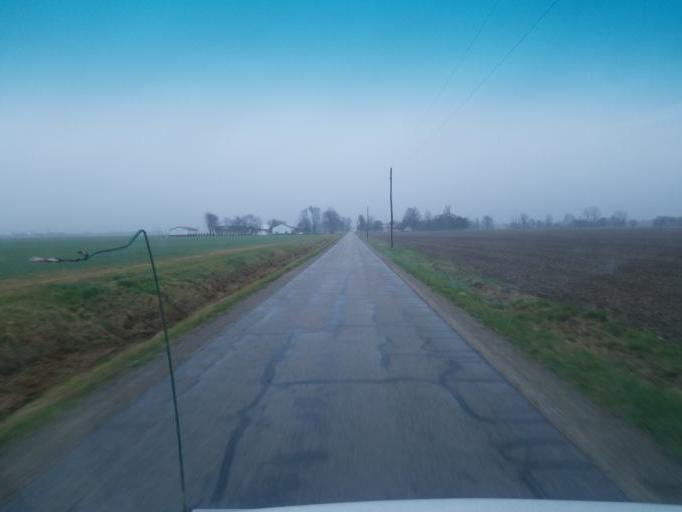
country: US
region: Ohio
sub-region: Henry County
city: Napoleon
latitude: 41.4135
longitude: -84.2135
